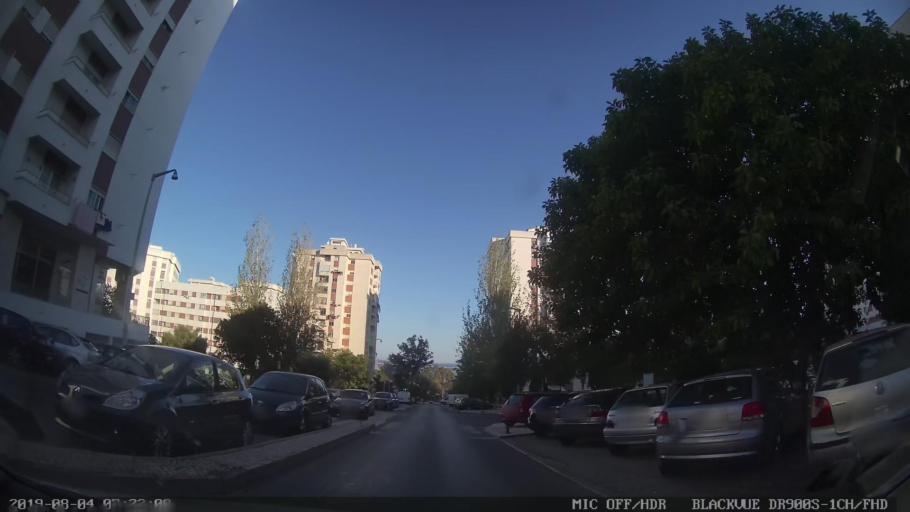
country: PT
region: Lisbon
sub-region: Vila Franca de Xira
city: Povoa de Santa Iria
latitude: 38.8584
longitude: -9.0705
